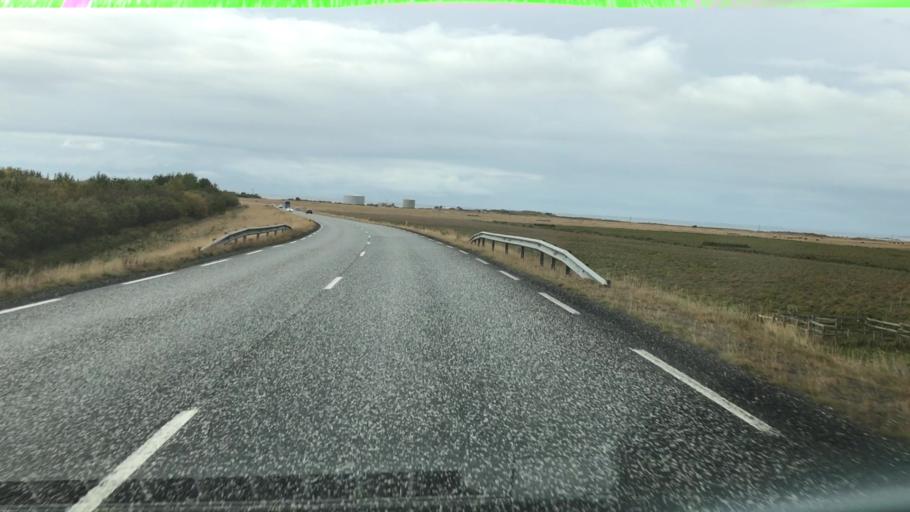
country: IS
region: West
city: Akranes
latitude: 64.3252
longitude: -22.0173
